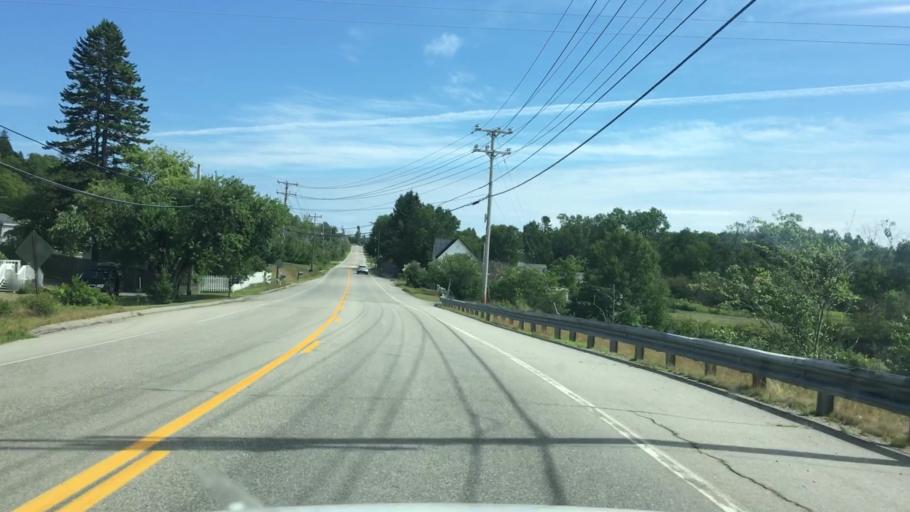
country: US
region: Maine
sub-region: Washington County
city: Eastport
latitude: 44.9193
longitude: -67.0153
